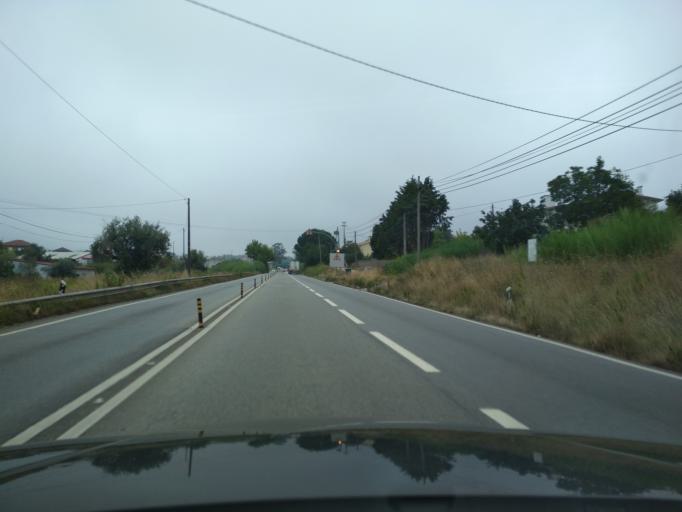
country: PT
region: Aveiro
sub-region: Mealhada
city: Pampilhosa do Botao
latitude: 40.2848
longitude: -8.4458
